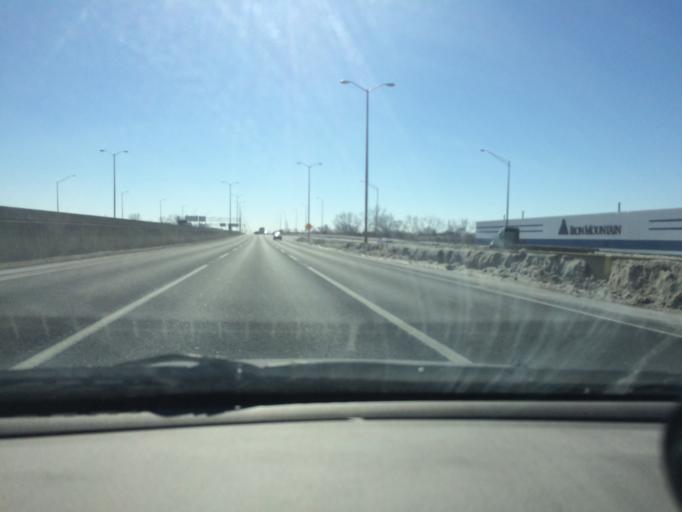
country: US
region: Illinois
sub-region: DuPage County
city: Glendale Heights
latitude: 41.9229
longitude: -88.0380
